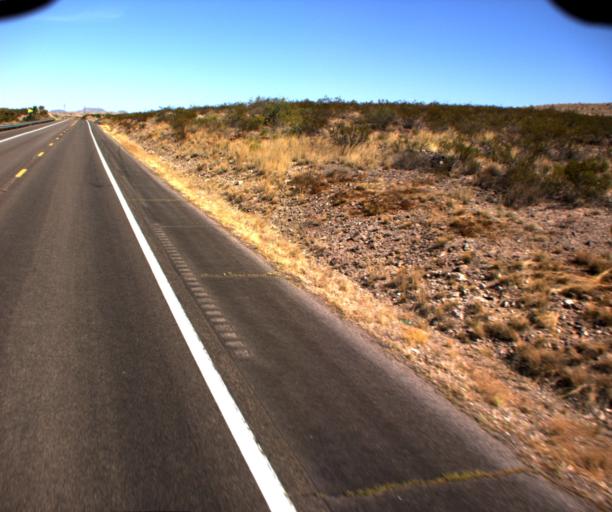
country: US
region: Arizona
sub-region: Greenlee County
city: Clifton
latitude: 32.7365
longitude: -109.1981
